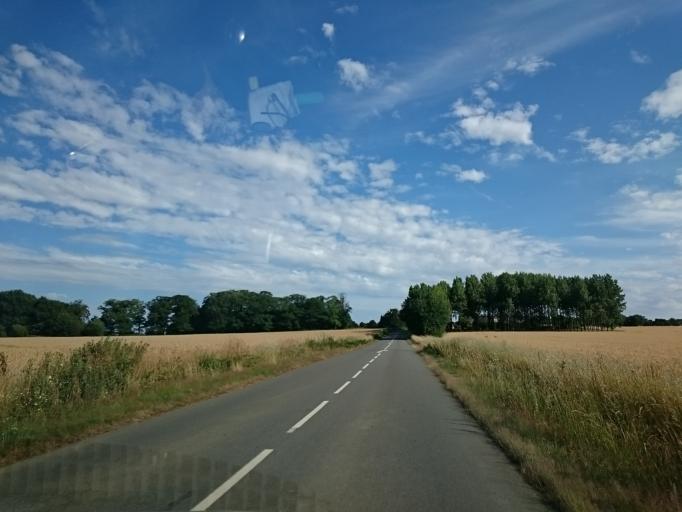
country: FR
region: Brittany
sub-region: Departement d'Ille-et-Vilaine
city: Chanteloup
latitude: 47.9129
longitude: -1.6165
